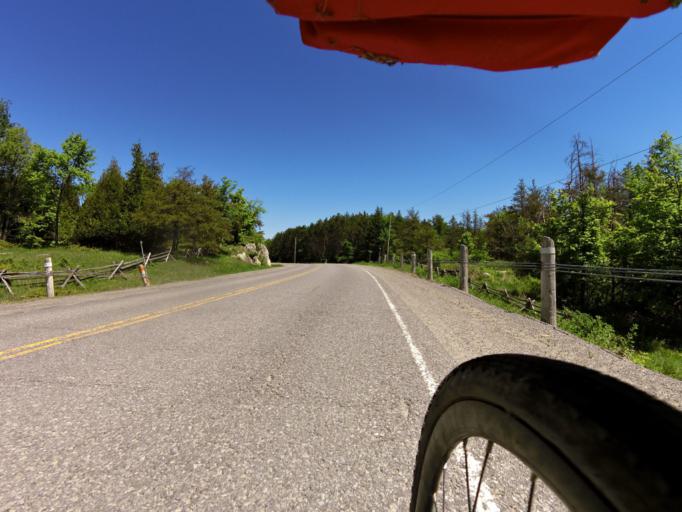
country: CA
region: Ontario
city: Carleton Place
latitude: 45.1834
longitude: -76.3636
